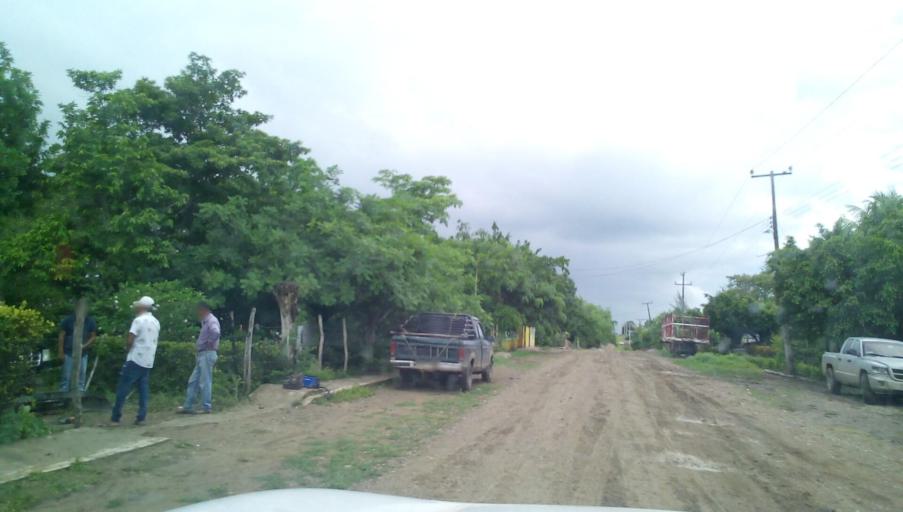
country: MX
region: Veracruz
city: Panuco
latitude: 21.8009
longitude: -98.1025
